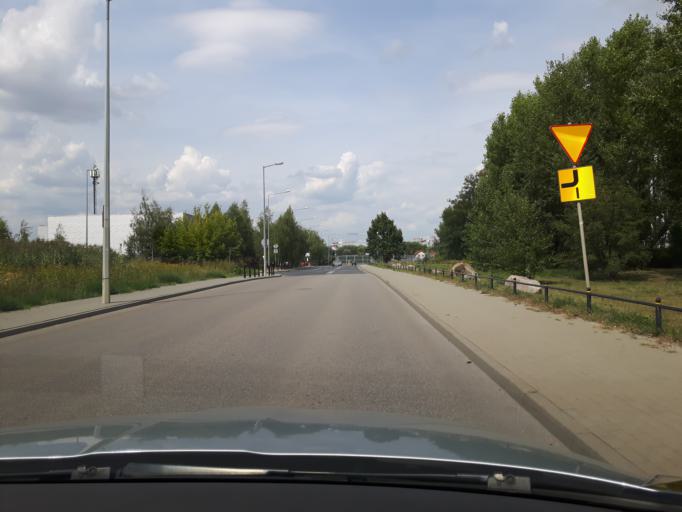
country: PL
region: Masovian Voivodeship
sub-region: Warszawa
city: Wlochy
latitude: 52.1542
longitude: 20.9945
